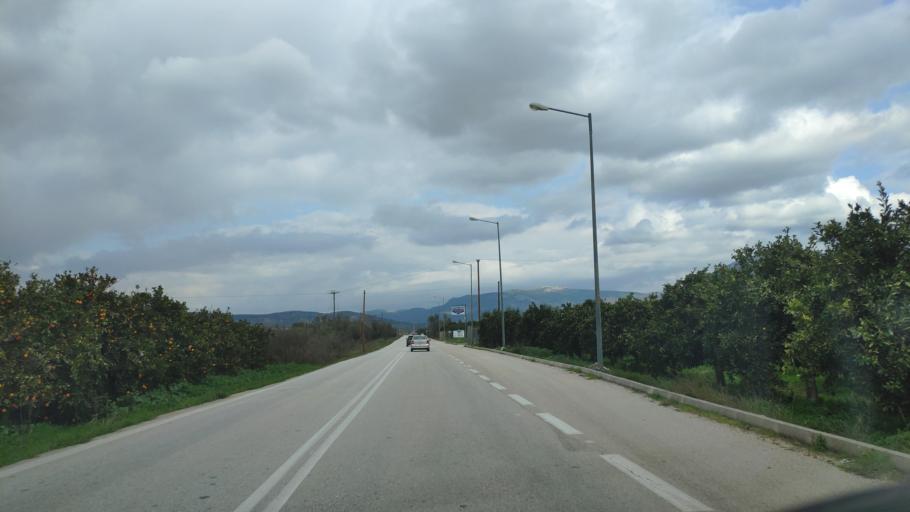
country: GR
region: Peloponnese
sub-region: Nomos Argolidos
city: Koutsopodi
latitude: 37.6958
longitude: 22.7218
